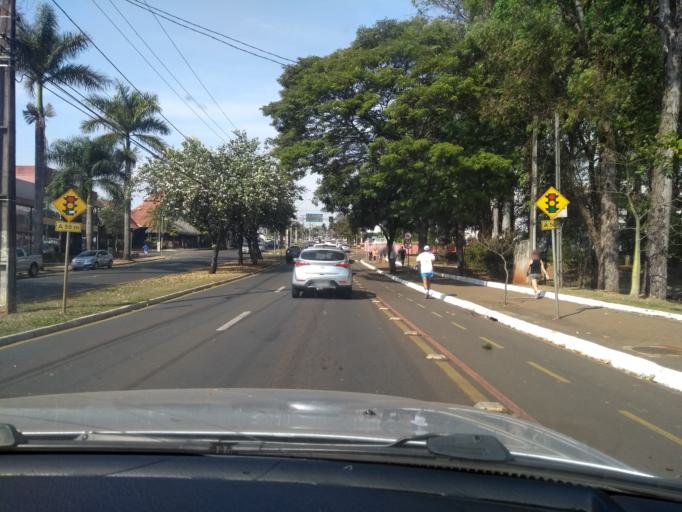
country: BR
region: Parana
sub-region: Londrina
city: Londrina
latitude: -23.3300
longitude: -51.1678
